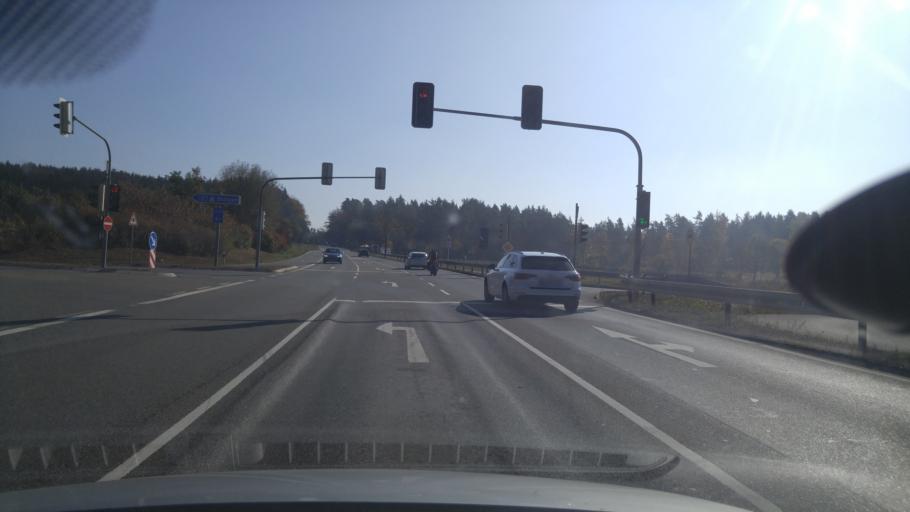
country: DE
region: Baden-Wuerttemberg
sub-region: Karlsruhe Region
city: Empfingen
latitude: 48.3842
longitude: 8.7256
